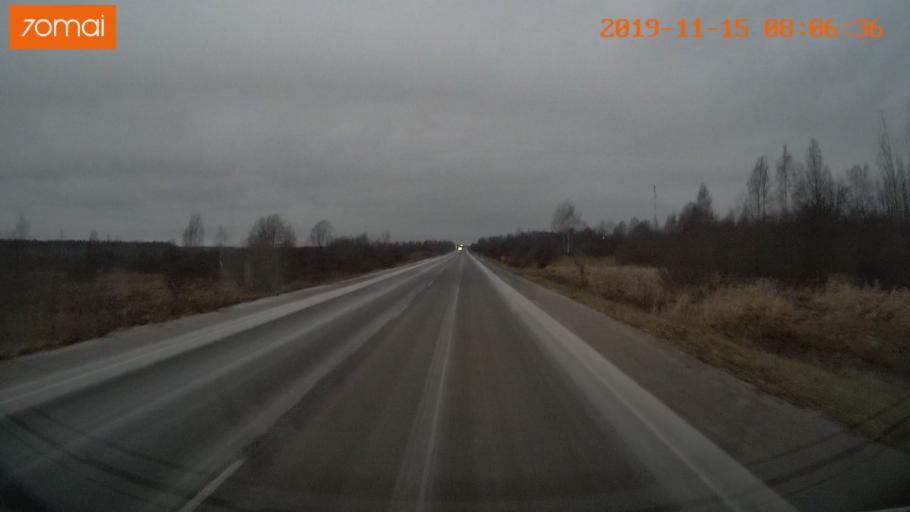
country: RU
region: Vologda
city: Cherepovets
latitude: 59.0229
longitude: 38.0347
